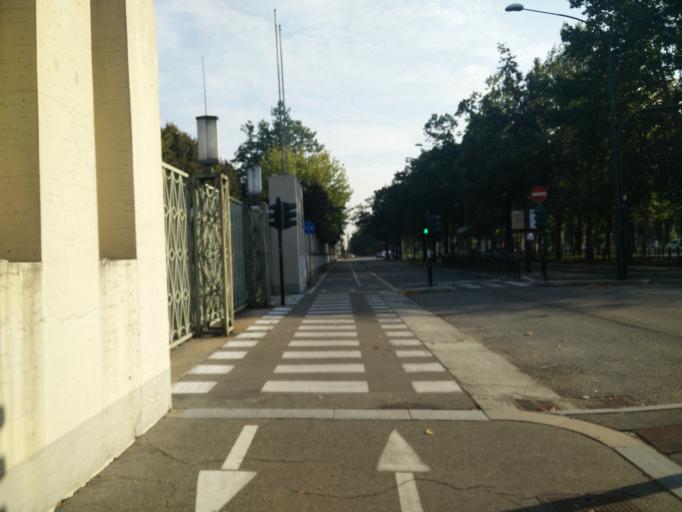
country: IT
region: Piedmont
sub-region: Provincia di Torino
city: Gerbido
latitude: 45.0290
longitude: 7.6386
